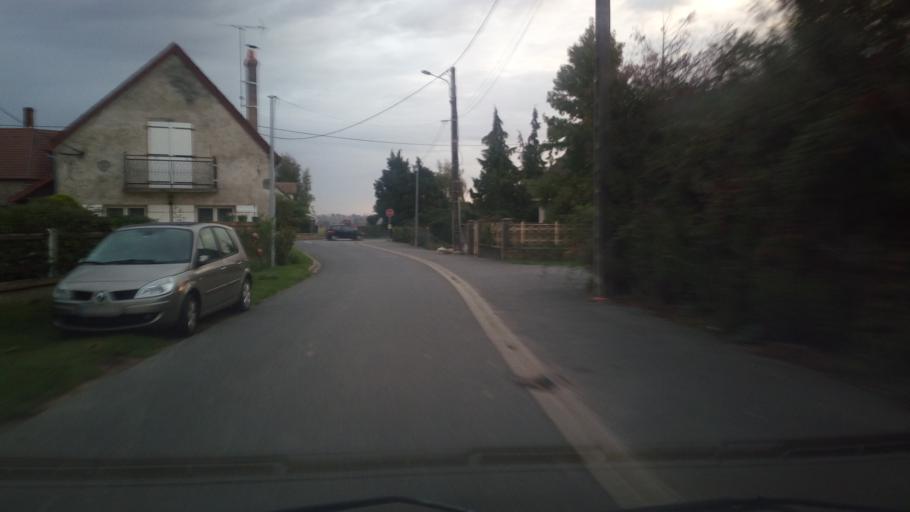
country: FR
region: Centre
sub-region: Departement du Loiret
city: Poilly-lez-Gien
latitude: 47.6805
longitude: 2.5877
